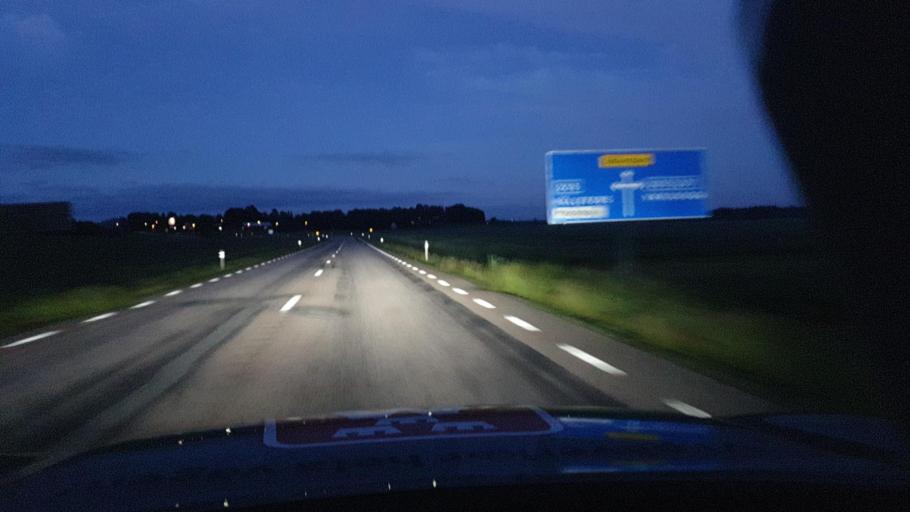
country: SE
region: OErebro
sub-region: Karlskoga Kommun
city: Karlskoga
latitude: 59.3803
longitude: 14.4935
